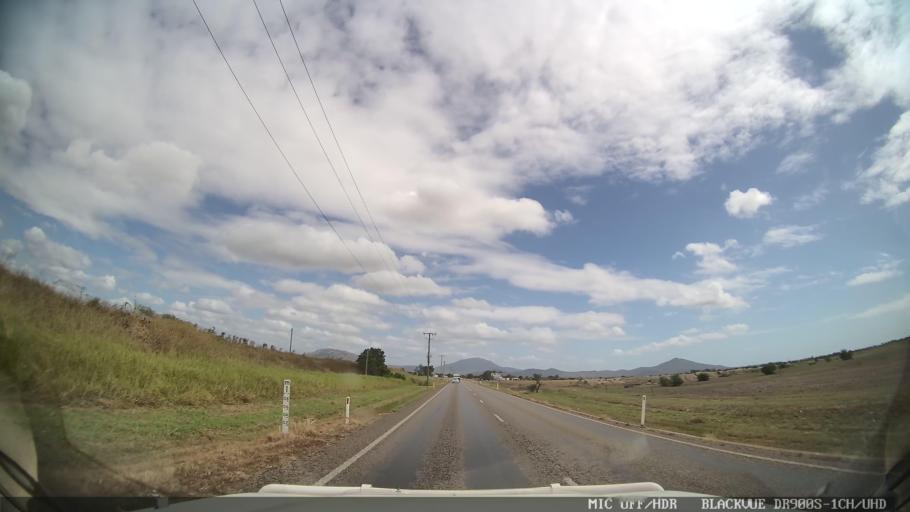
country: AU
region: Queensland
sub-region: Whitsunday
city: Bowen
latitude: -20.0152
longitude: 148.1792
